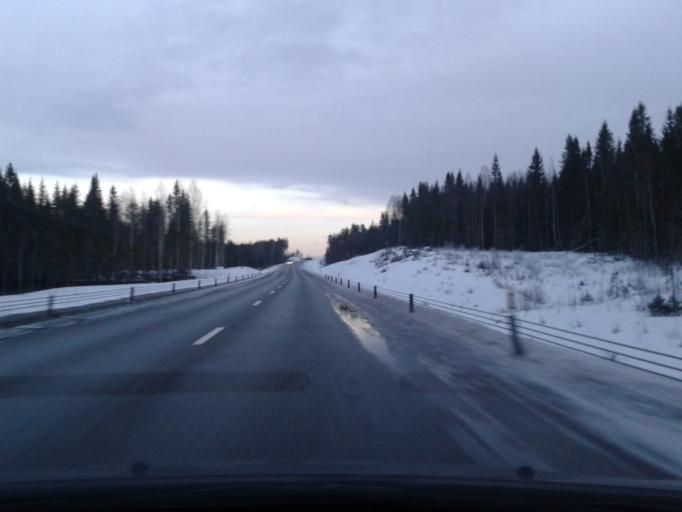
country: SE
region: Vaesternorrland
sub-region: Kramfors Kommun
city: Bollstabruk
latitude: 63.0680
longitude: 17.5778
